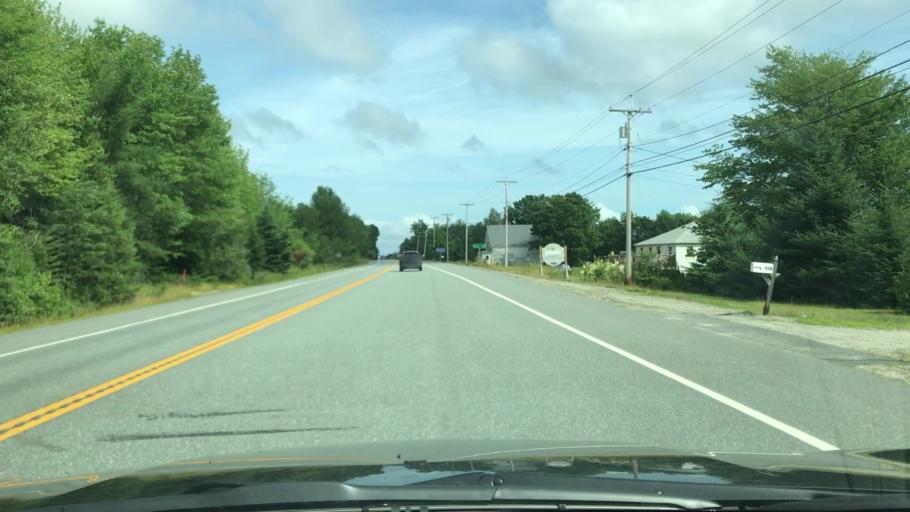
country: US
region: Maine
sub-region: Hancock County
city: Surry
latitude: 44.5458
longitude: -68.5196
